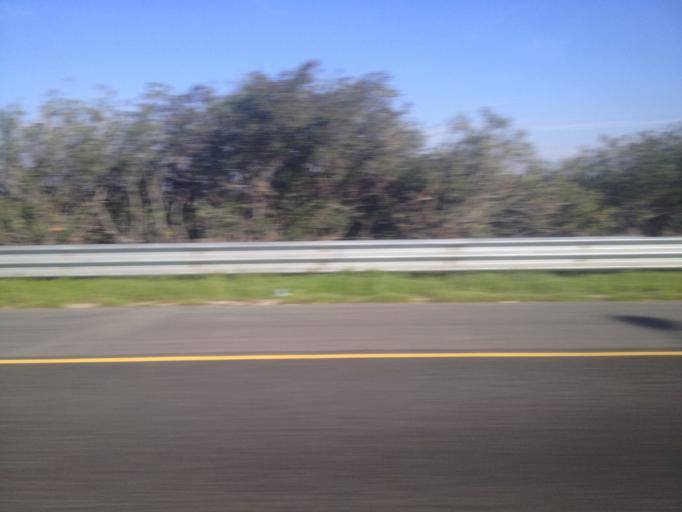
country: US
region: California
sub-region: Fresno County
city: Fowler
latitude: 36.6380
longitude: -119.6971
